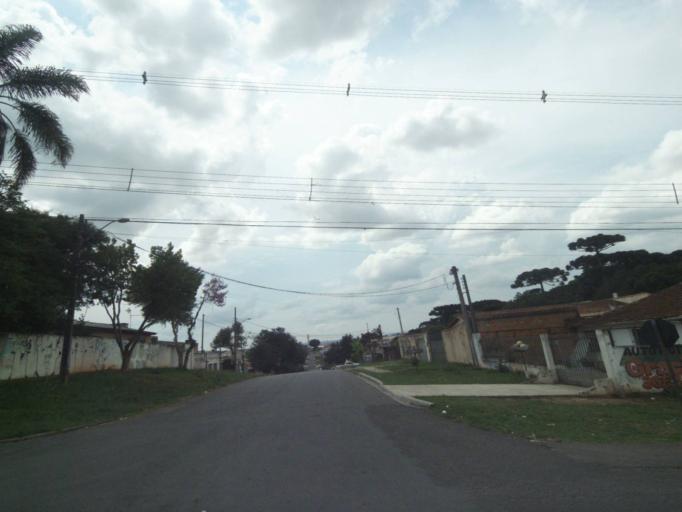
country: BR
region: Parana
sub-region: Pinhais
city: Pinhais
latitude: -25.3982
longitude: -49.1975
